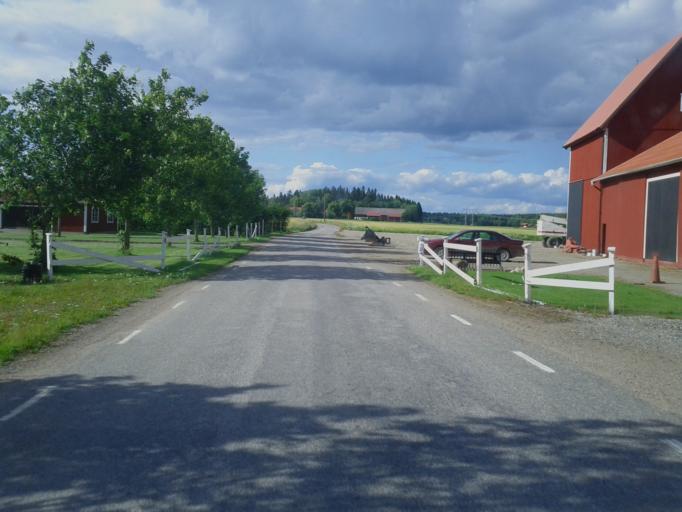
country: SE
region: Vaestmanland
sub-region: Sala Kommun
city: Sala
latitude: 59.9181
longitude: 16.5046
